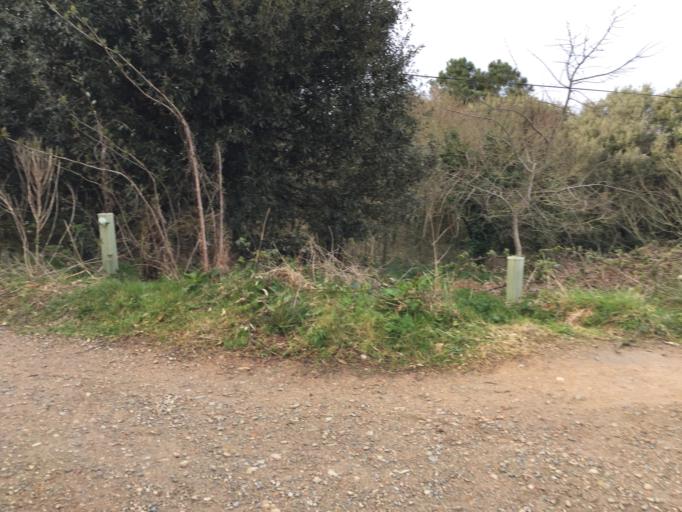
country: JE
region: St Helier
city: Saint Helier
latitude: 49.1863
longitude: -2.2150
